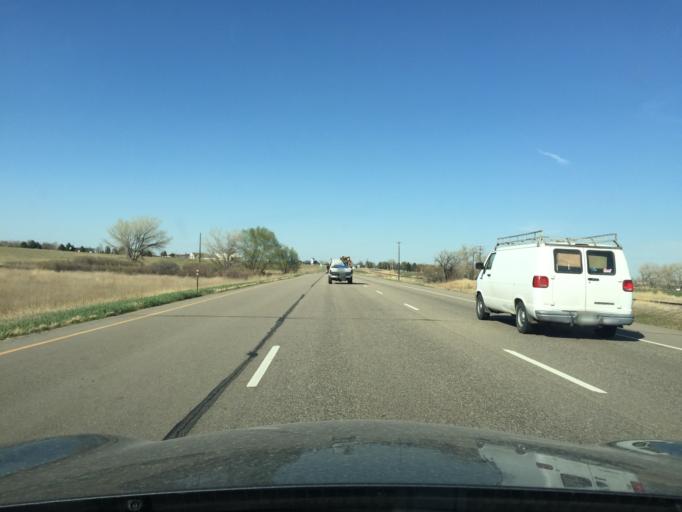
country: US
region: Colorado
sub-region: Boulder County
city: Niwot
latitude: 40.1326
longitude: -105.1377
